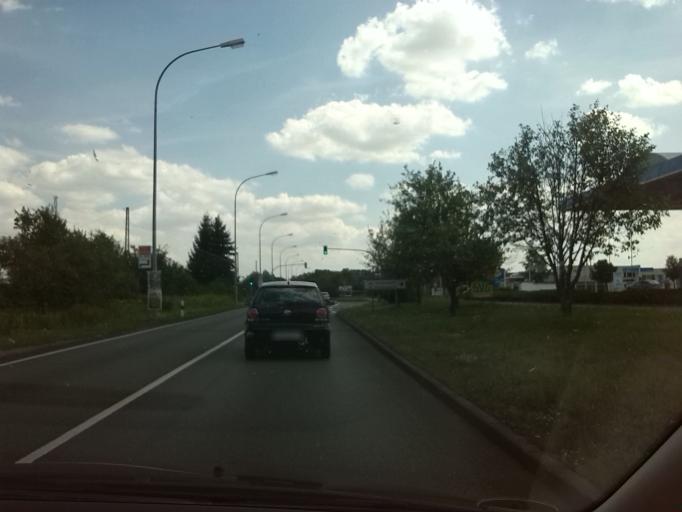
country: DE
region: Saxony
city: Borna
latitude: 51.1164
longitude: 12.4860
